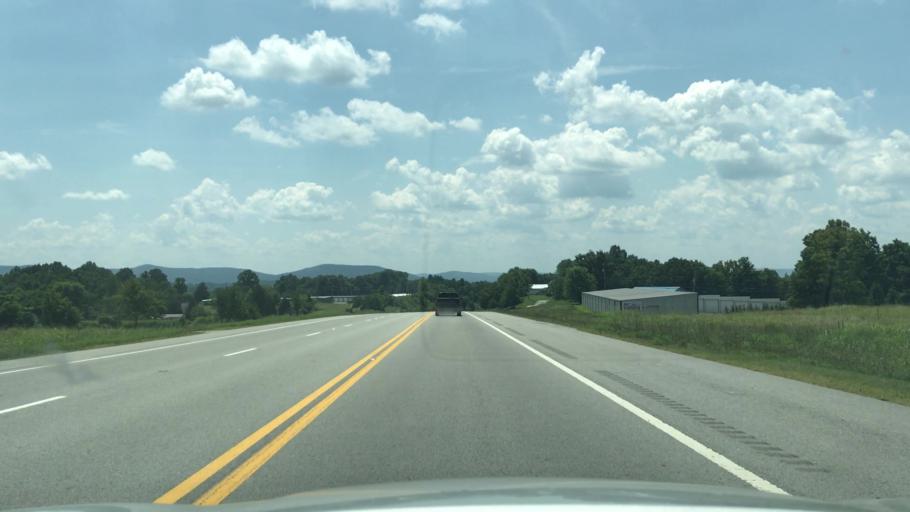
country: US
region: Tennessee
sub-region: Pickett County
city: Byrdstown
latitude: 36.5447
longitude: -85.1630
